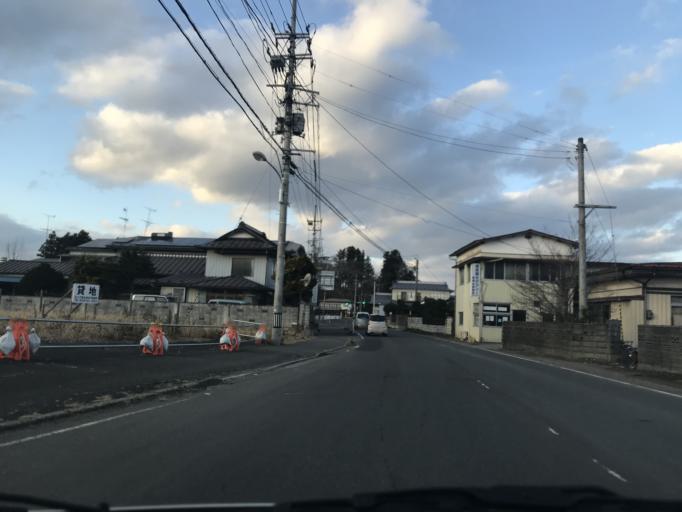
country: JP
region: Miyagi
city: Furukawa
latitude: 38.6595
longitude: 141.0112
